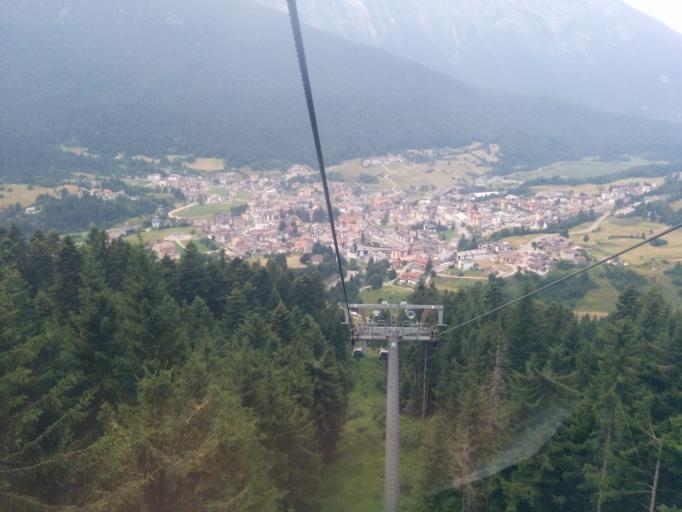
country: IT
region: Trentino-Alto Adige
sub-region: Provincia di Trento
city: Andalo
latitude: 46.1568
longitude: 11.0115
